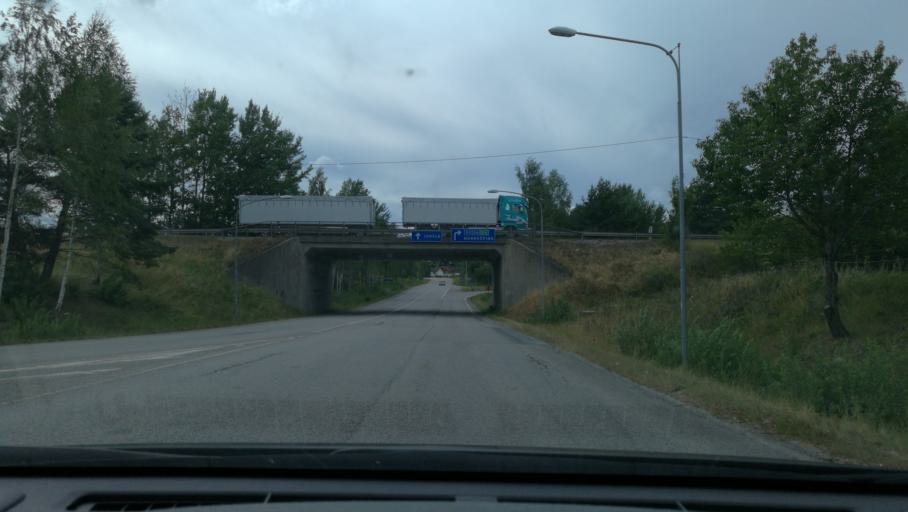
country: SE
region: OEstergoetland
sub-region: Norrkopings Kommun
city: Jursla
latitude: 58.6567
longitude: 16.1714
